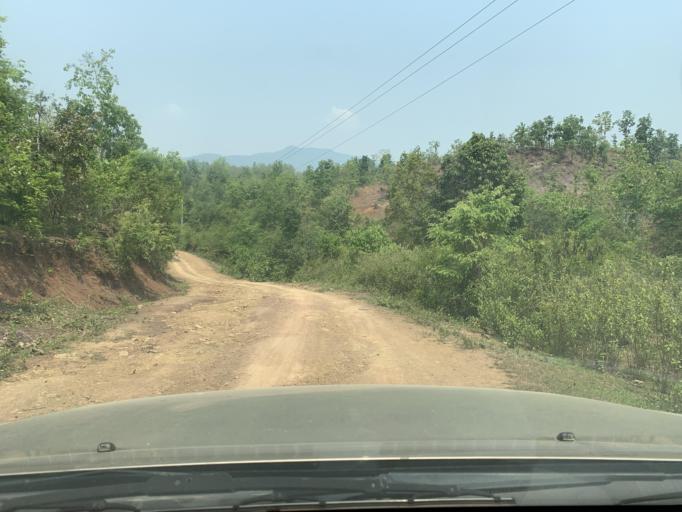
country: LA
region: Louangphabang
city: Louangphabang
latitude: 19.9491
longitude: 102.1327
